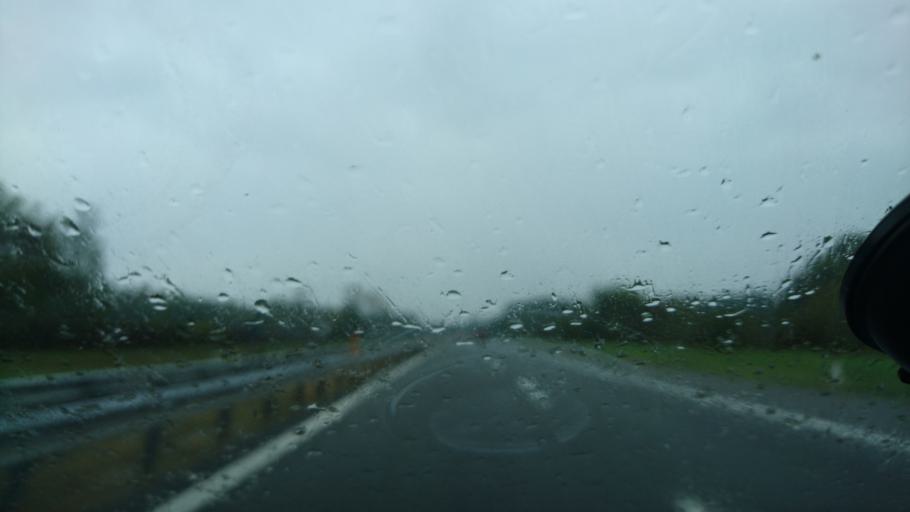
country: IT
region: Piedmont
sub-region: Provincia di Novara
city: Fontaneto D'Agogna
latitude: 45.6398
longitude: 8.4580
